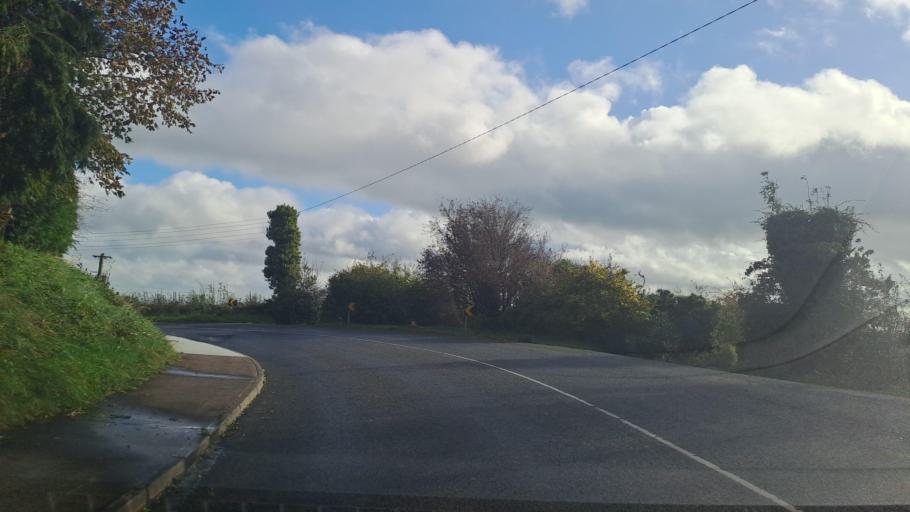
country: IE
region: Ulster
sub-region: County Monaghan
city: Monaghan
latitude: 54.1281
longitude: -6.9136
